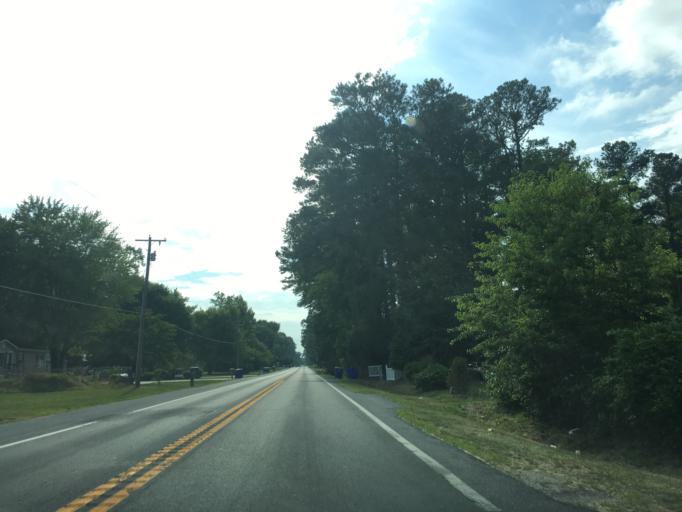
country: US
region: Delaware
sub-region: Sussex County
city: Georgetown
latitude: 38.7432
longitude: -75.4324
